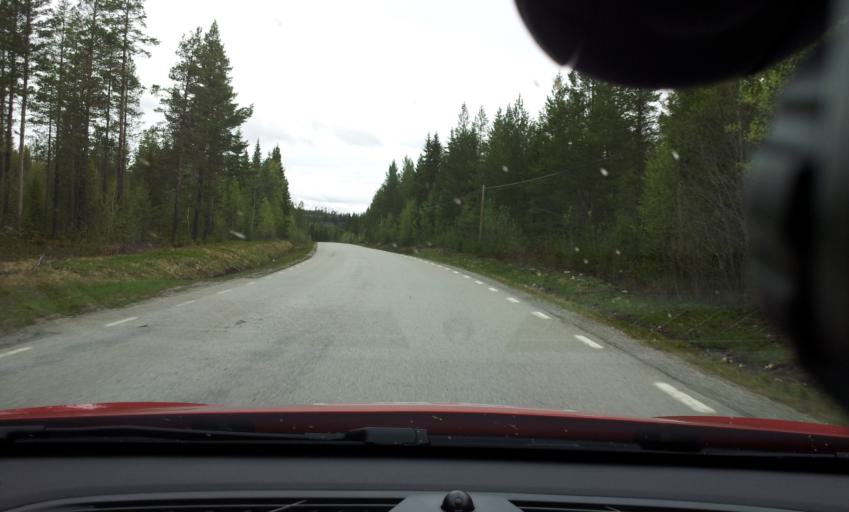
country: SE
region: Jaemtland
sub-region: Bergs Kommun
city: Hoverberg
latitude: 62.7495
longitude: 14.5756
